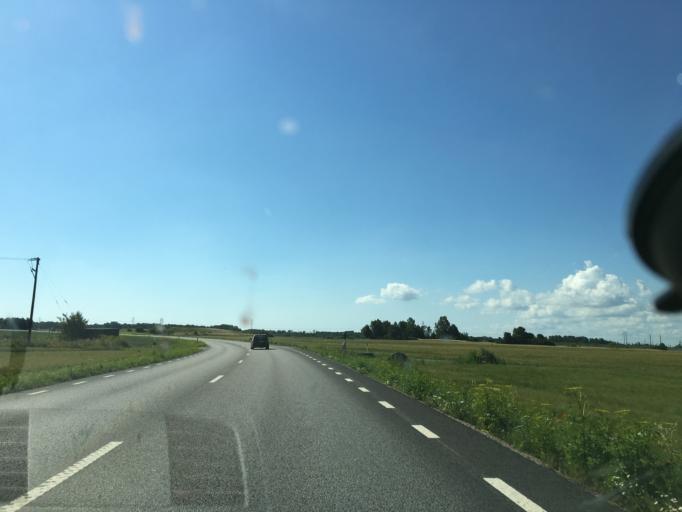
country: SE
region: Skane
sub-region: Kristianstads Kommun
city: Norra Asum
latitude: 55.9471
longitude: 14.2092
